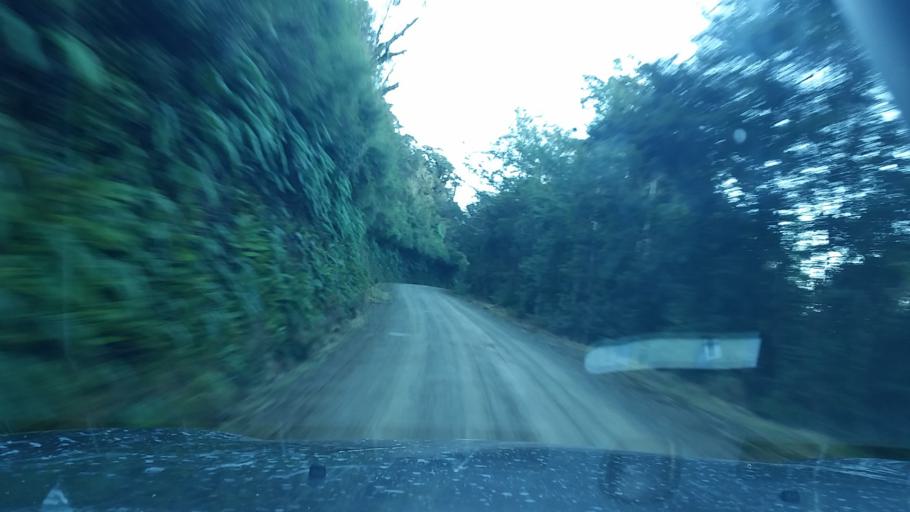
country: NZ
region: Marlborough
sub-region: Marlborough District
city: Picton
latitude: -41.0892
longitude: 174.1546
